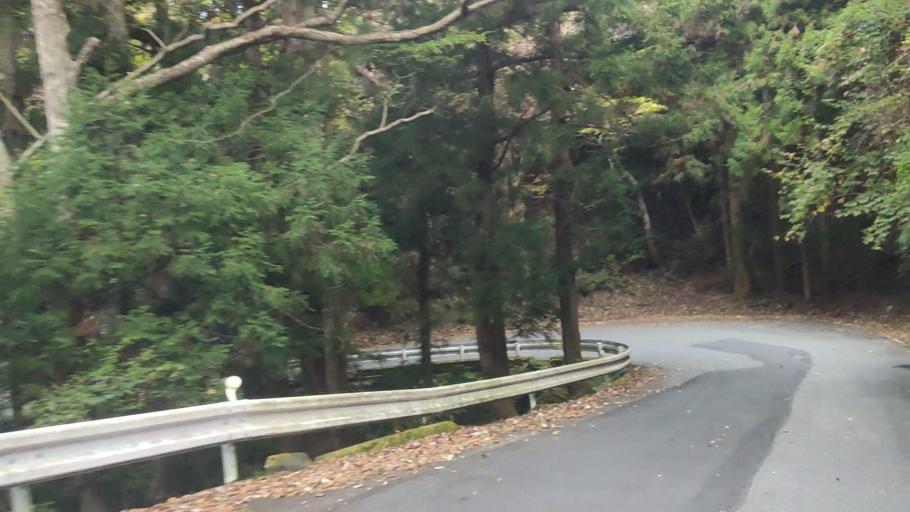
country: JP
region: Shizuoka
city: Ito
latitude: 34.9537
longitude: 139.0521
